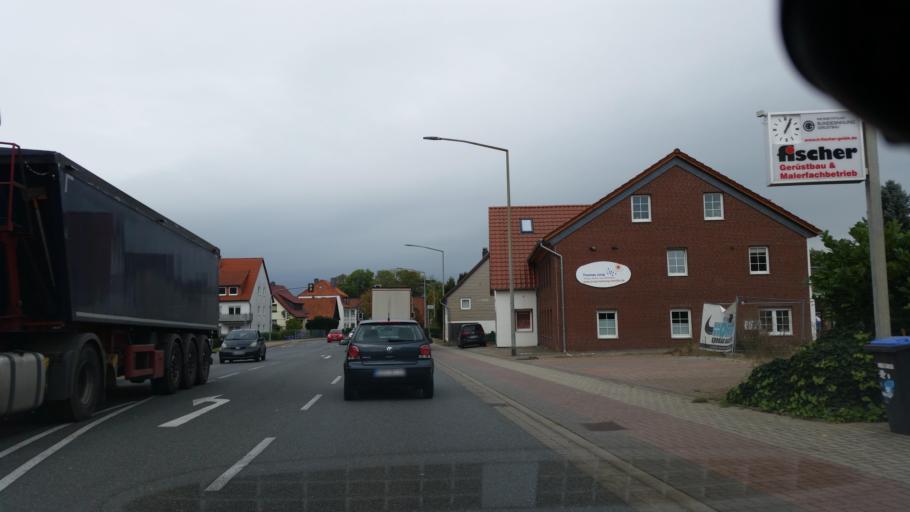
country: DE
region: Lower Saxony
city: Giesen
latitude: 52.1931
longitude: 9.9220
